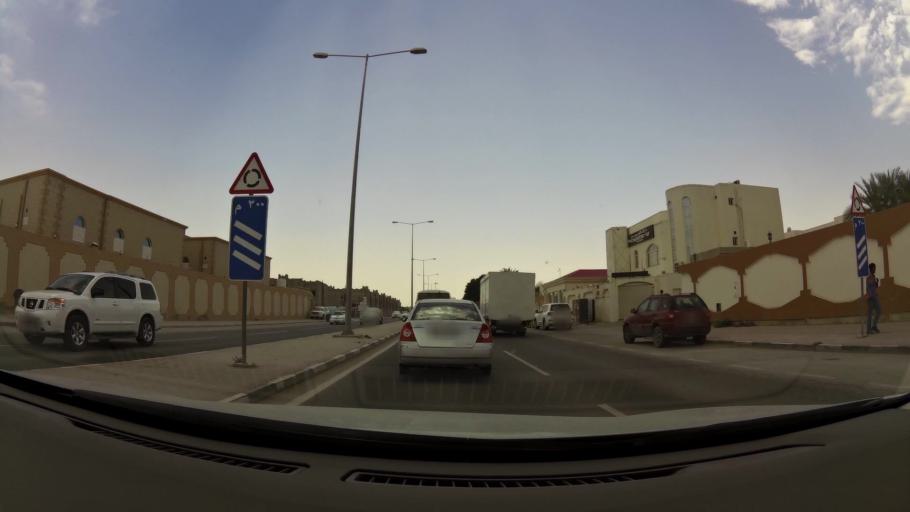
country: QA
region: Baladiyat ar Rayyan
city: Ar Rayyan
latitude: 25.2533
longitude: 51.4180
